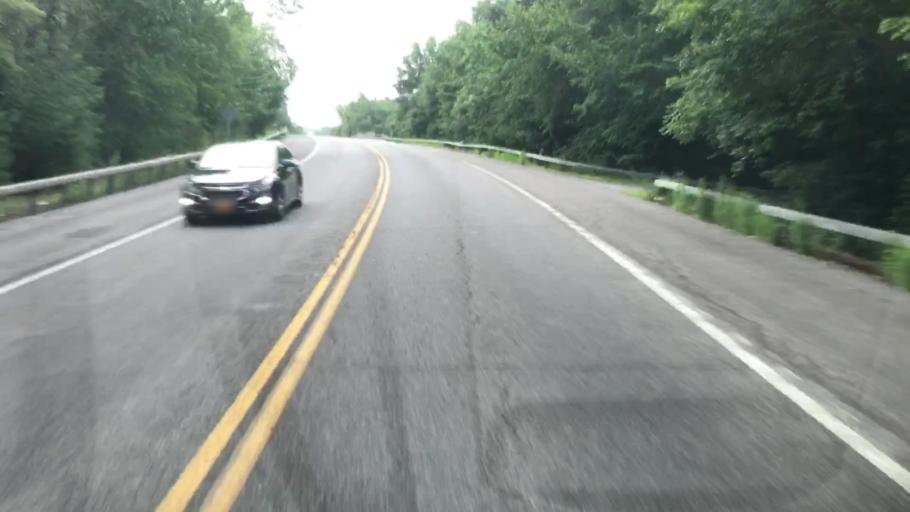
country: US
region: New York
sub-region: Onondaga County
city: Liverpool
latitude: 43.1726
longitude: -76.1992
